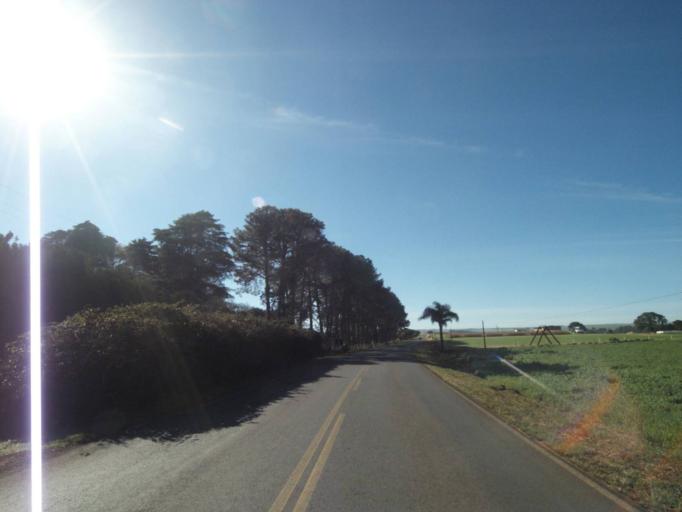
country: BR
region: Parana
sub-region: Tibagi
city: Tibagi
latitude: -24.5250
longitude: -50.3775
